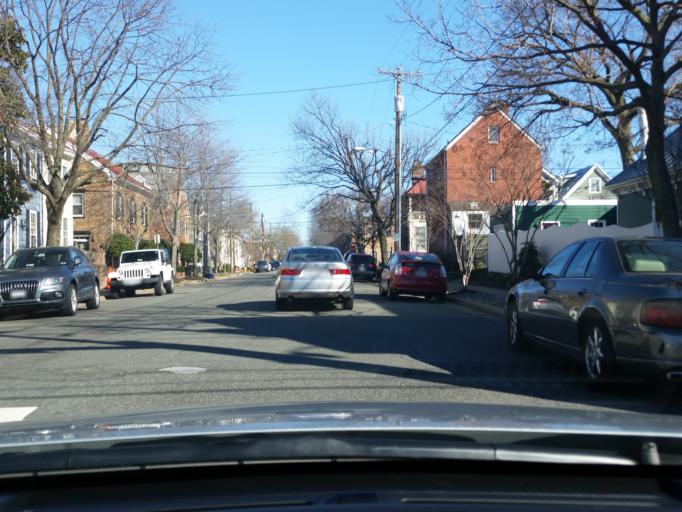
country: US
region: Virginia
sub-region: City of Alexandria
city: Alexandria
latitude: 38.8100
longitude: -77.0494
